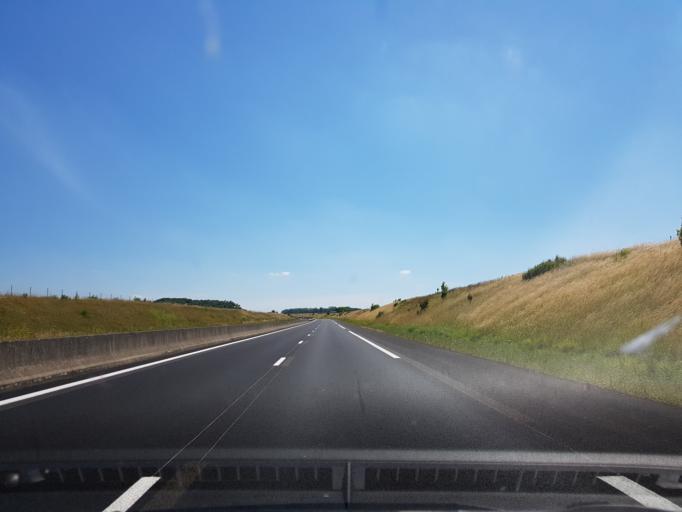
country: FR
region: Picardie
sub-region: Departement de l'Aisne
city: Holnon
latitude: 49.8428
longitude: 3.2003
